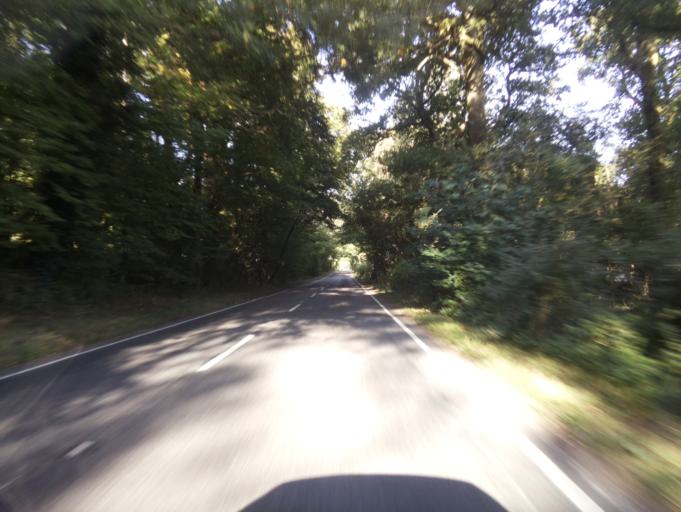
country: GB
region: England
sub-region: Hampshire
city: Four Marks
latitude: 51.0616
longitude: -1.0286
